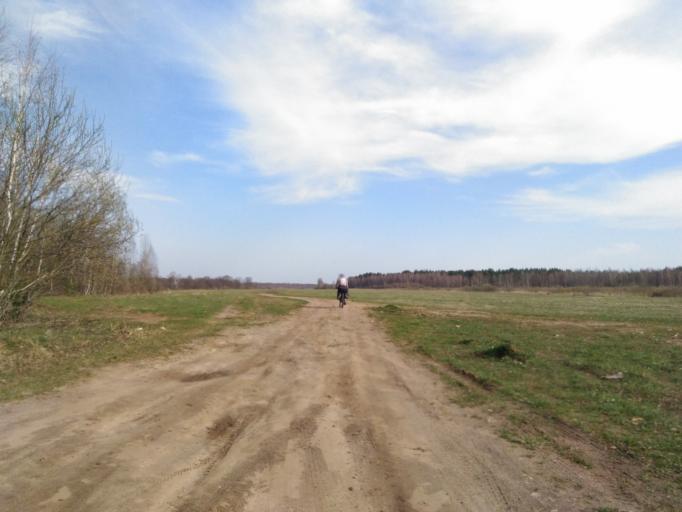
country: RU
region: Vladimir
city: Petushki
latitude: 55.9022
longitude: 39.4666
